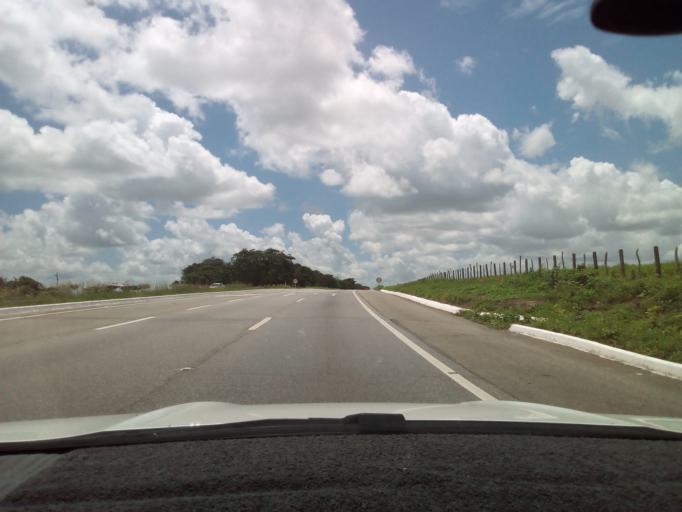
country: BR
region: Paraiba
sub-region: Pilar
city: Pilar
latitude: -7.1880
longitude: -35.2120
